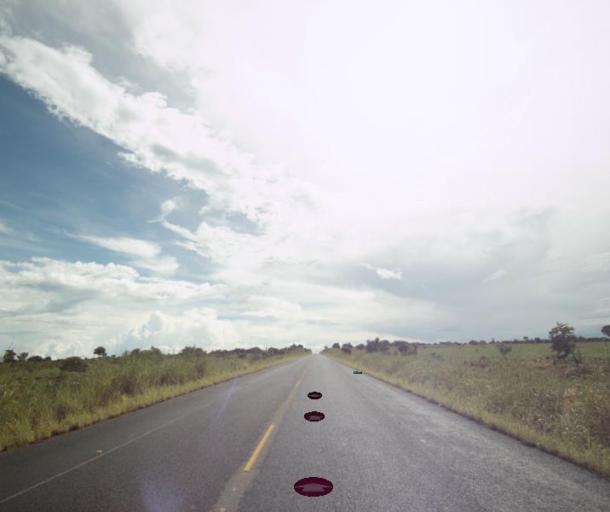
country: BR
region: Goias
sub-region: Sao Miguel Do Araguaia
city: Sao Miguel do Araguaia
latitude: -13.3009
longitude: -50.2942
